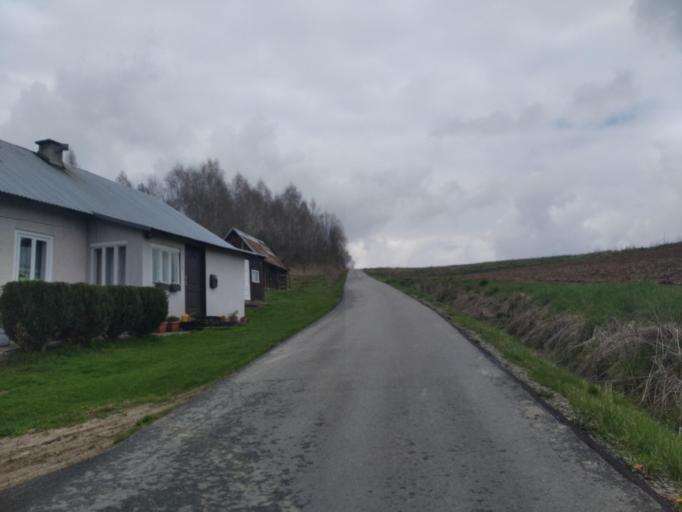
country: PL
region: Subcarpathian Voivodeship
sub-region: Powiat strzyzowski
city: Wysoka Strzyzowska
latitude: 49.8840
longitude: 21.7134
